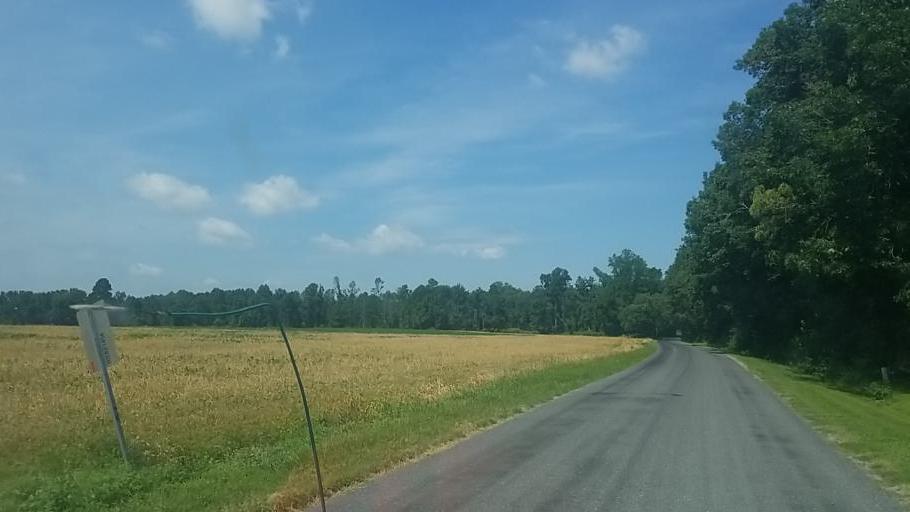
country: US
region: Maryland
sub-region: Caroline County
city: Denton
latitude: 38.8793
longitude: -75.7787
